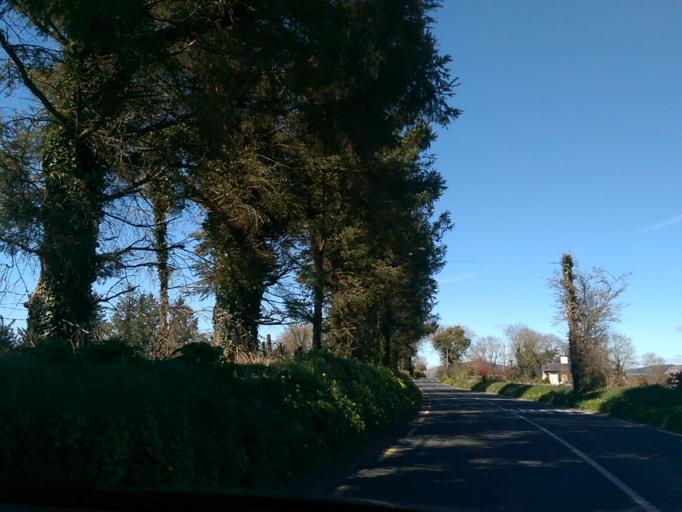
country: IE
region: Leinster
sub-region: Wicklow
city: Baltinglass
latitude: 52.8838
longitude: -6.5901
